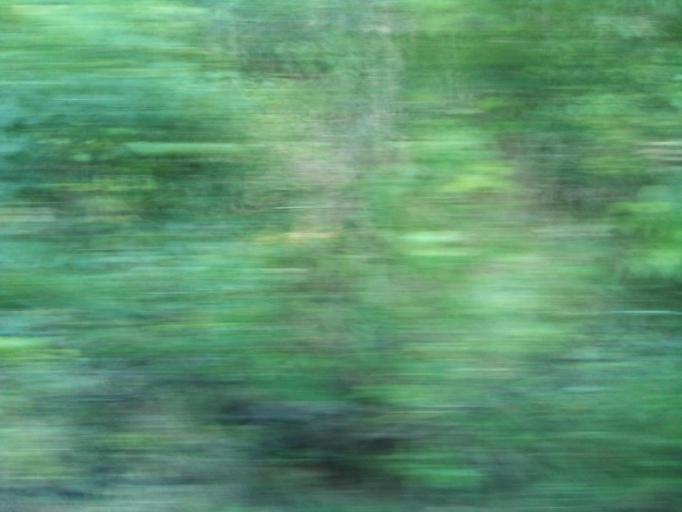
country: BR
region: Minas Gerais
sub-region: Caete
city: Caete
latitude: -19.8926
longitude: -43.7434
